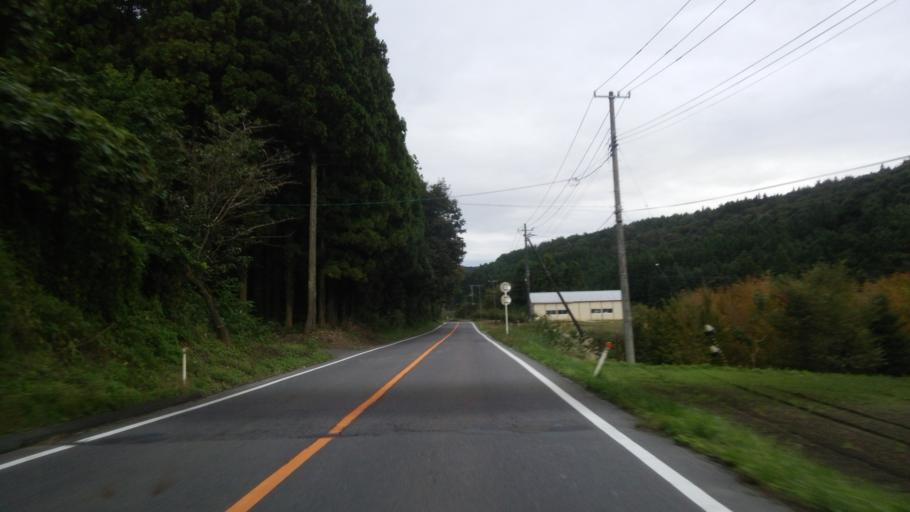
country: JP
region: Fukushima
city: Sukagawa
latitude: 37.2139
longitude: 140.2496
